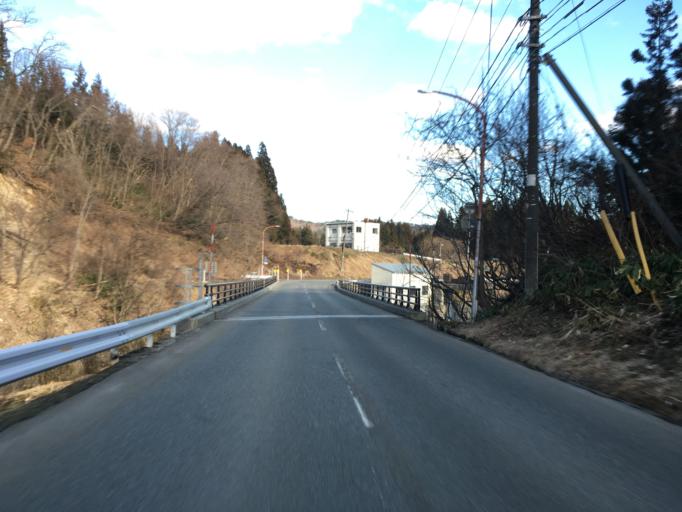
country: JP
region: Yamagata
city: Nagai
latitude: 37.9804
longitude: 139.9373
